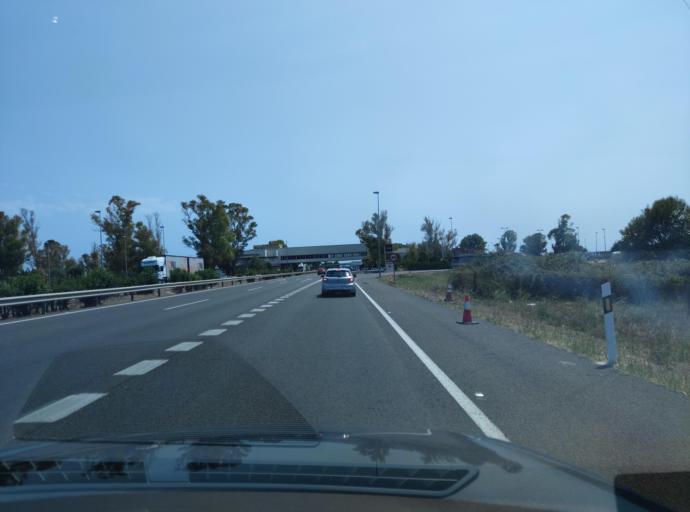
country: ES
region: Valencia
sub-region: Provincia de Castello
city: Alquerias del Nino Perdido
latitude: 39.8671
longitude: -0.1224
